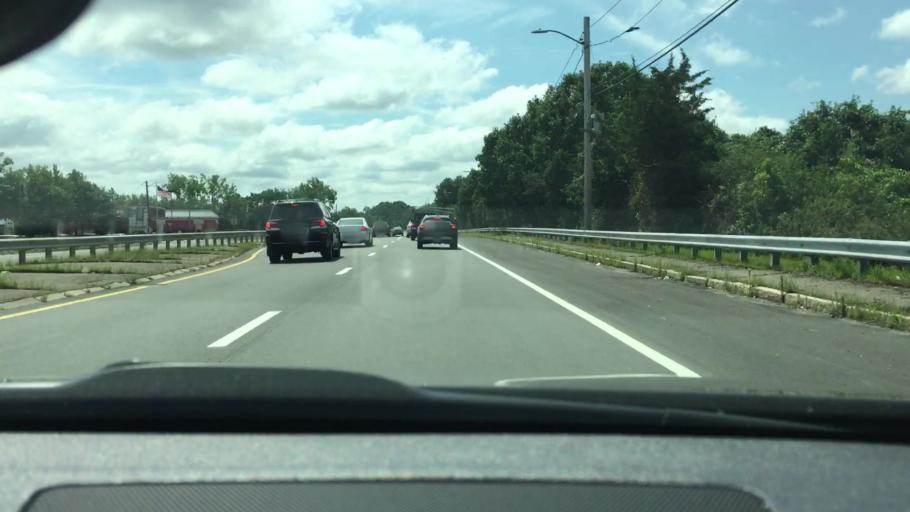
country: US
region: Massachusetts
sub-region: Norfolk County
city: Dedham
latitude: 42.2579
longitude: -71.1703
